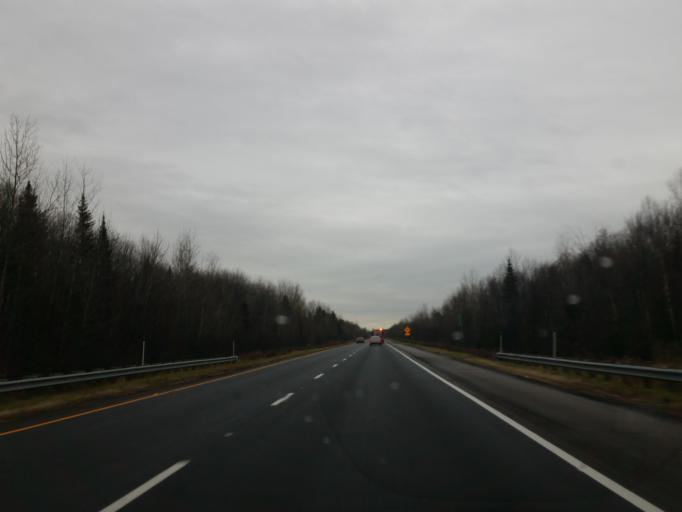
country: CA
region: Quebec
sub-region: Capitale-Nationale
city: Cap-Sante
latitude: 46.6977
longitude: -71.8311
